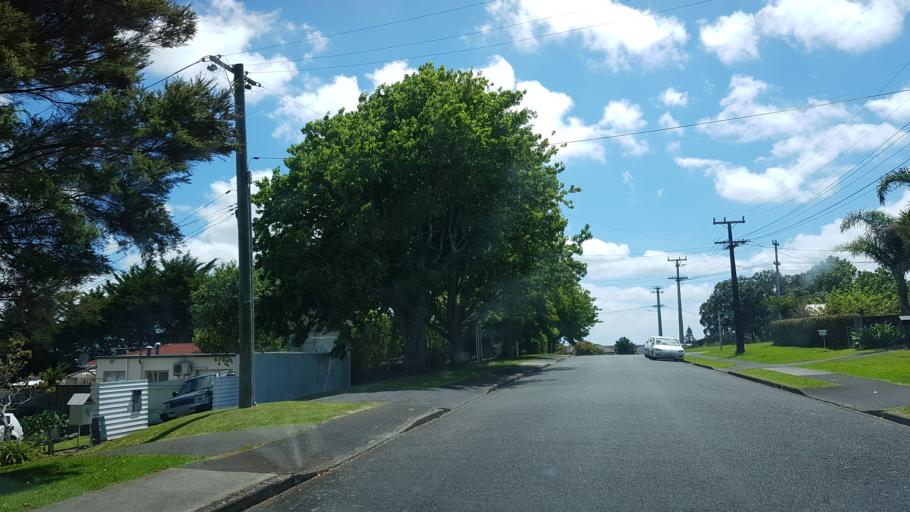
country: NZ
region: Auckland
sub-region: Auckland
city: North Shore
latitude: -36.7905
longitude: 174.7125
